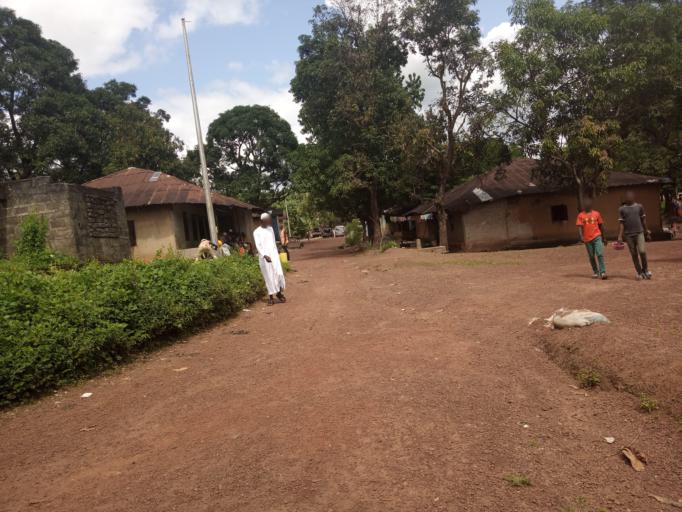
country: SL
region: Northern Province
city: Kamakwie
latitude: 9.4943
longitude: -12.2420
